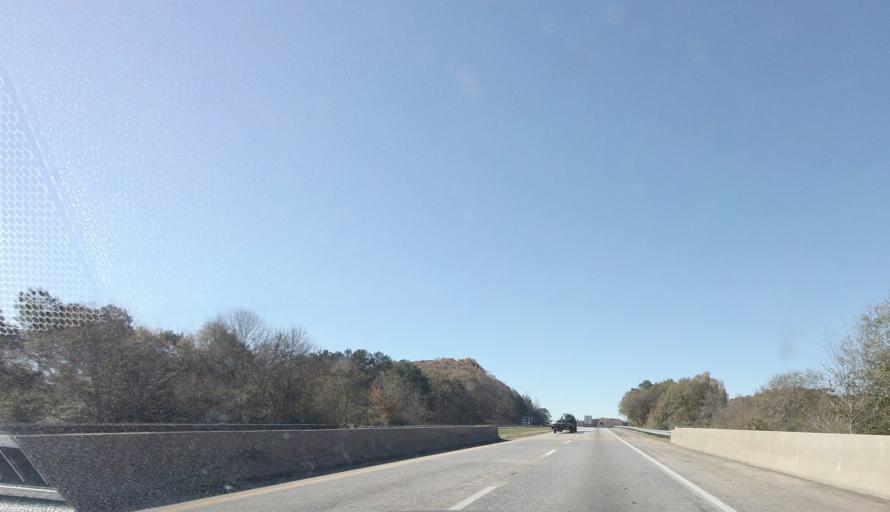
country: US
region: Alabama
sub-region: Calhoun County
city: Choccolocco
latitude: 33.6129
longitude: -85.7513
